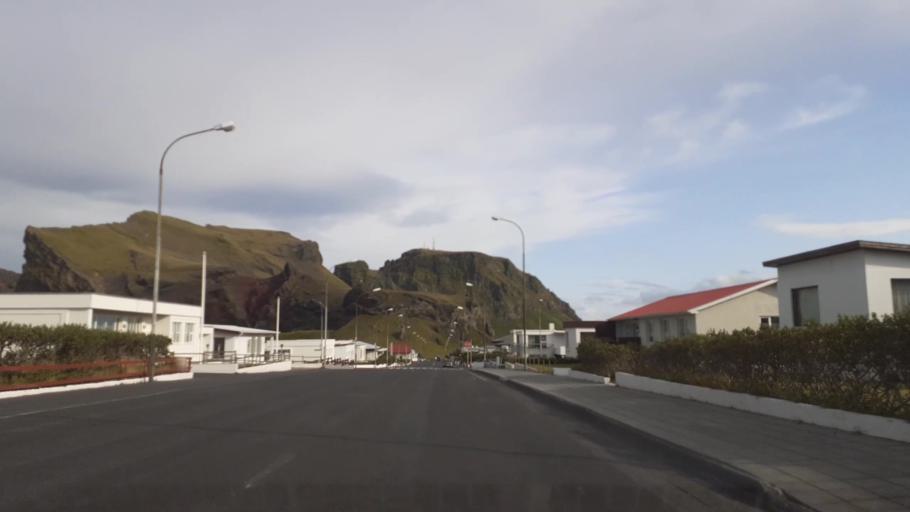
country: IS
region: South
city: Vestmannaeyjar
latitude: 63.4354
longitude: -20.2811
